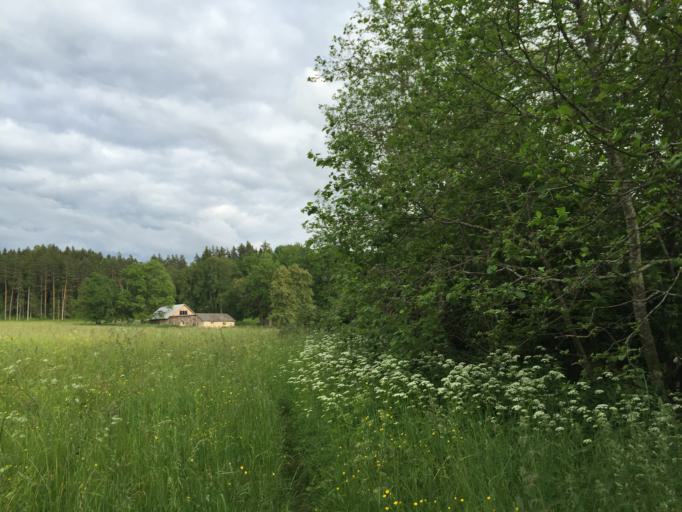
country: LV
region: Ligatne
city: Ligatne
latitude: 57.2449
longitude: 25.1464
